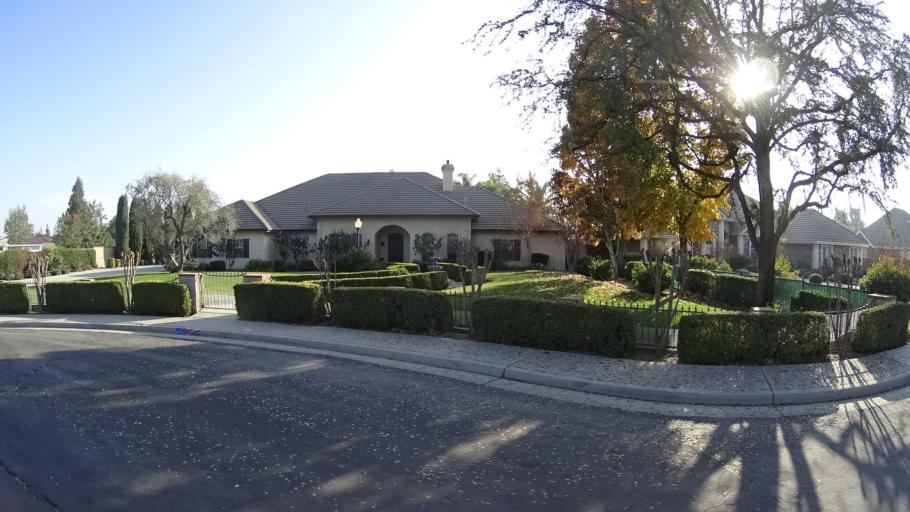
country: US
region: California
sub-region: Kern County
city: Rosedale
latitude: 35.3555
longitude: -119.1522
